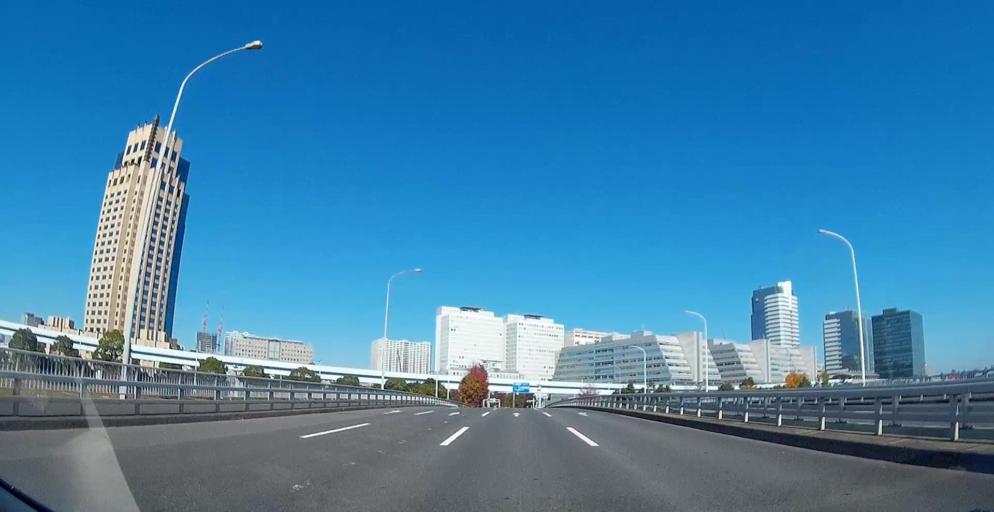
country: JP
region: Tokyo
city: Urayasu
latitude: 35.6271
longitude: 139.7890
